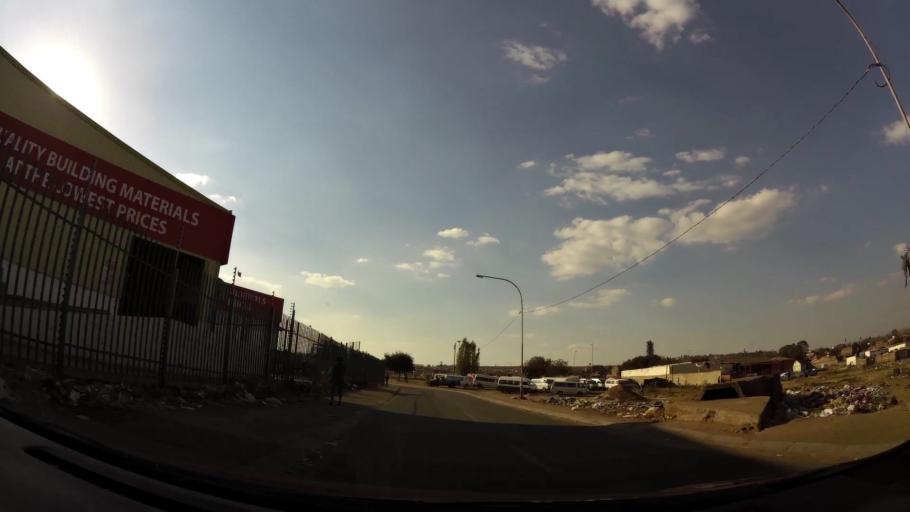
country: ZA
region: Gauteng
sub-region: City of Johannesburg Metropolitan Municipality
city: Roodepoort
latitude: -26.2153
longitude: 27.8756
